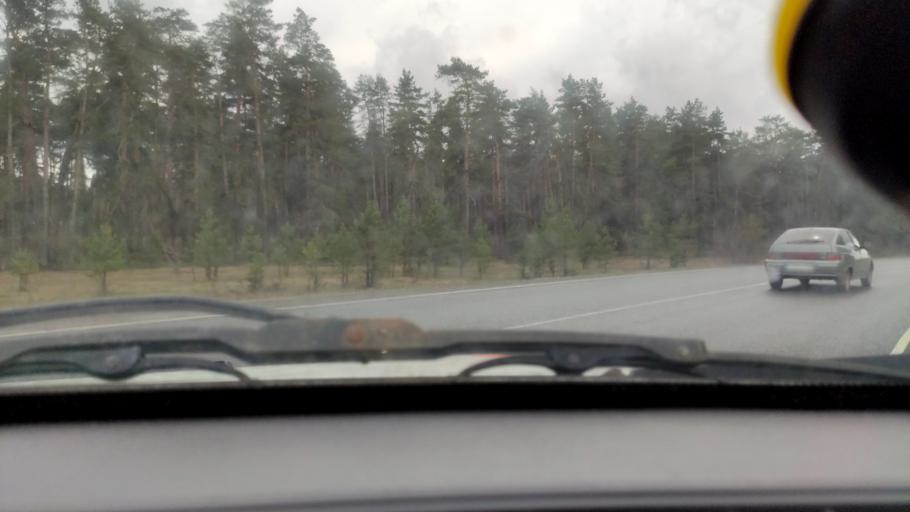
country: RU
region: Samara
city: Povolzhskiy
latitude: 53.6301
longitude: 49.6584
